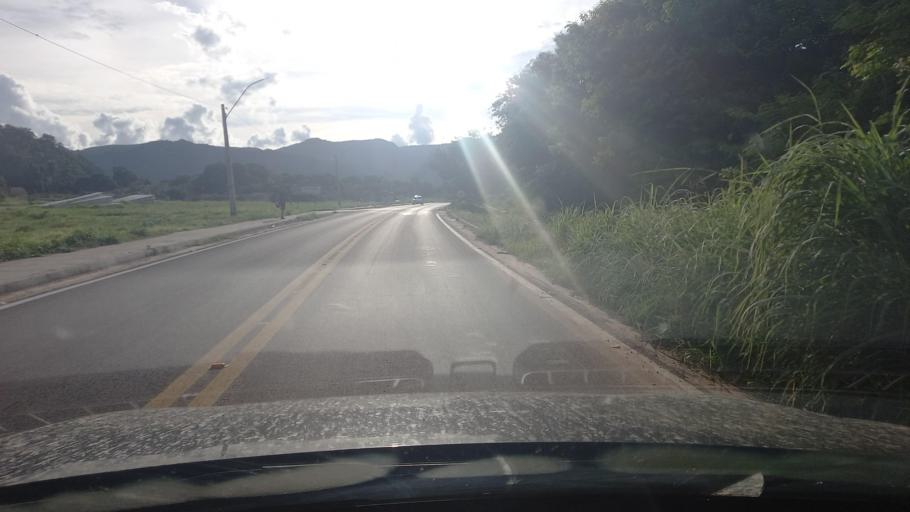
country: BR
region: Goias
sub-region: Cavalcante
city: Cavalcante
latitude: -13.7960
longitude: -47.4474
